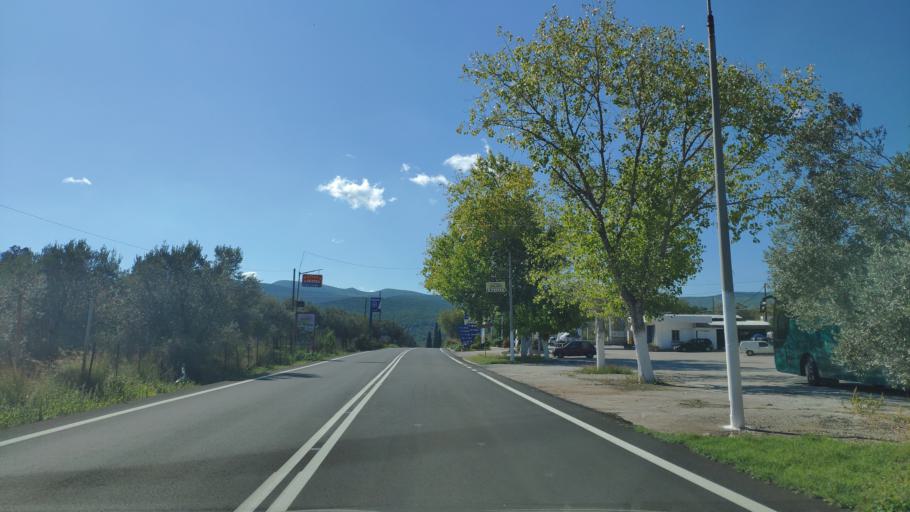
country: GR
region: Peloponnese
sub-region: Nomos Korinthias
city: Sofikon
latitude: 37.8034
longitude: 23.0803
